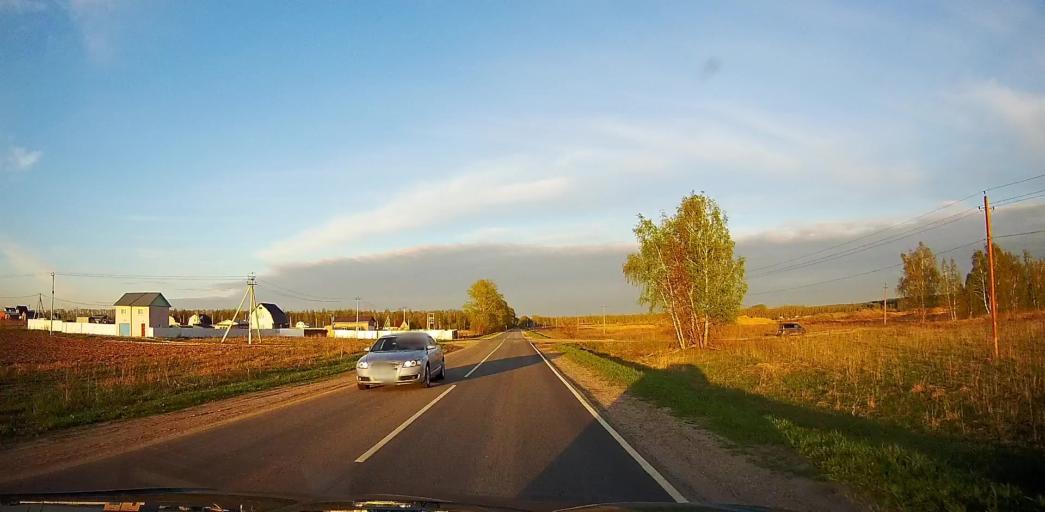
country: RU
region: Moskovskaya
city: Peski
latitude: 55.2103
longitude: 38.6926
